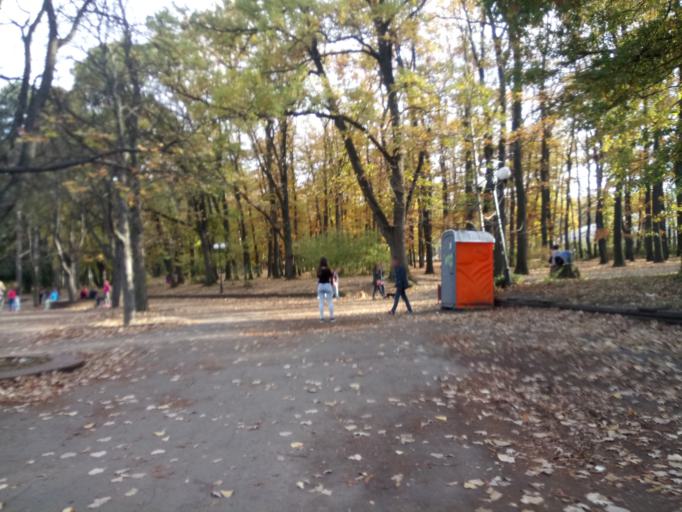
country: BG
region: Sofia-Capital
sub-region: Stolichna Obshtina
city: Sofia
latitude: 42.6852
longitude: 23.3418
